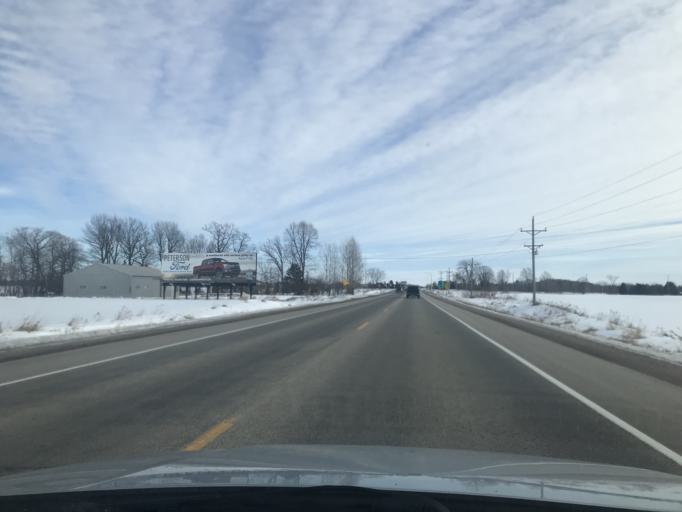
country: US
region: Wisconsin
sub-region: Oconto County
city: Gillett
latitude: 44.8962
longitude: -88.2527
